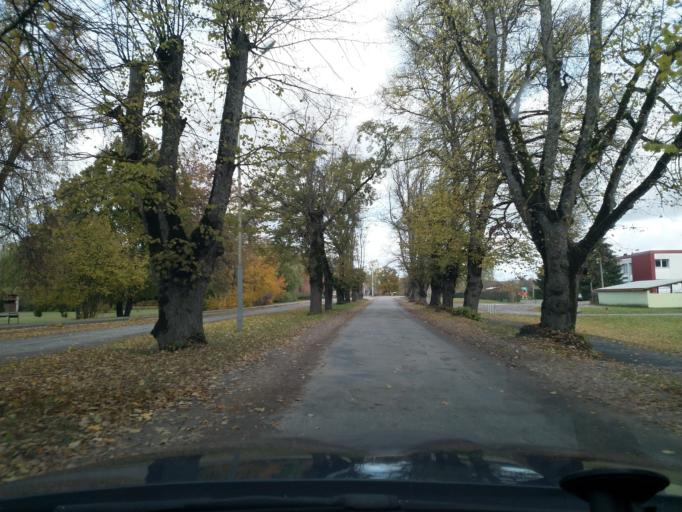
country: LV
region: Dundaga
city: Dundaga
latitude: 57.5072
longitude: 22.3497
